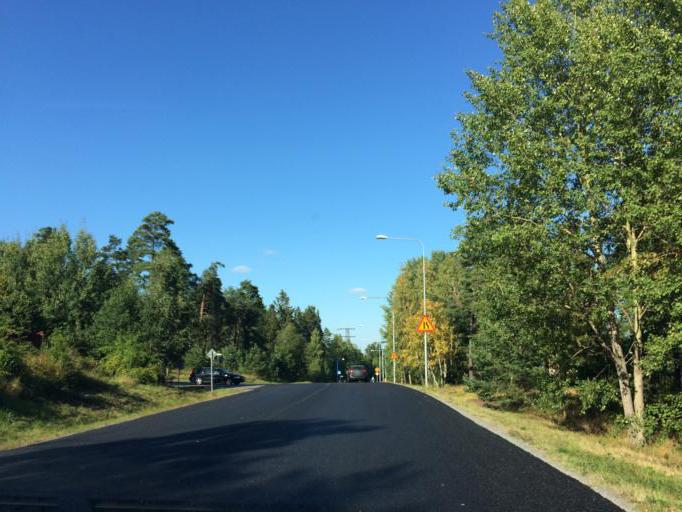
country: SE
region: Stockholm
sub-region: Upplands Vasby Kommun
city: Upplands Vaesby
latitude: 59.5022
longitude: 17.9485
